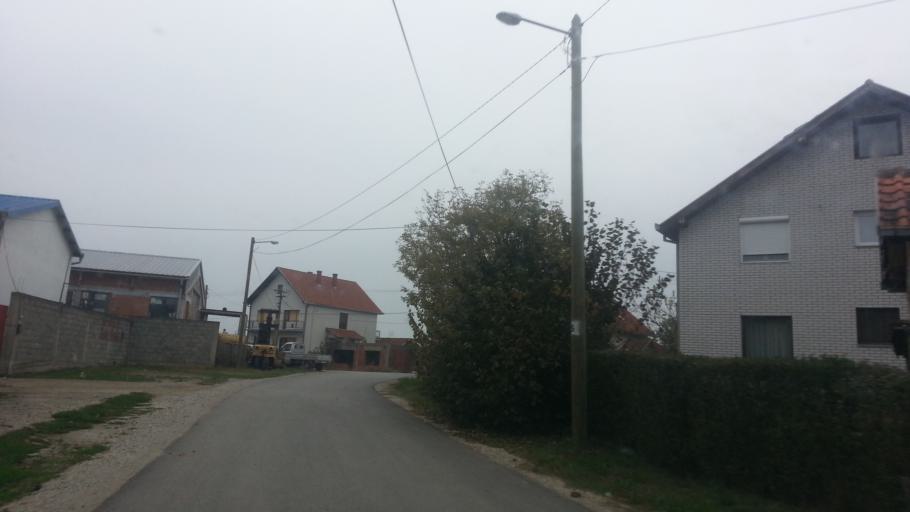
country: RS
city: Stari Banovci
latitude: 44.9819
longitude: 20.2712
